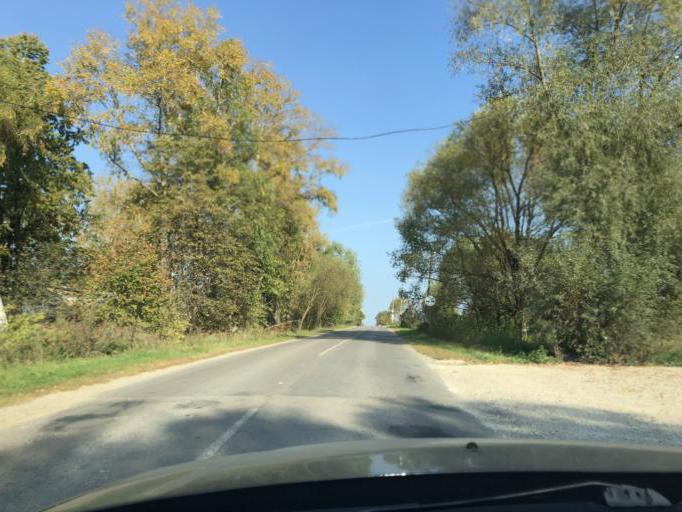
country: RU
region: Tula
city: Leninskiy
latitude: 54.3442
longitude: 37.3622
